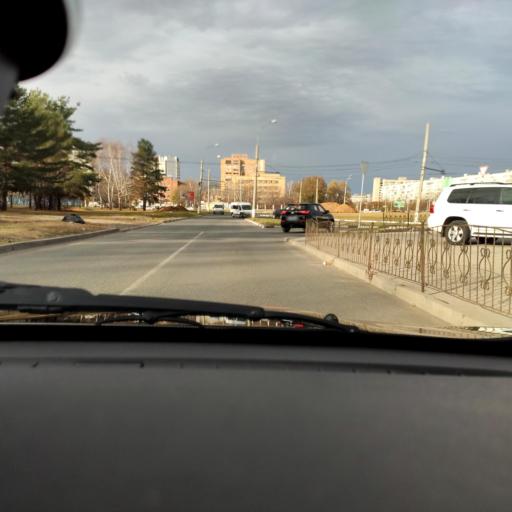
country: RU
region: Samara
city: Tol'yatti
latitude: 53.5239
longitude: 49.3280
